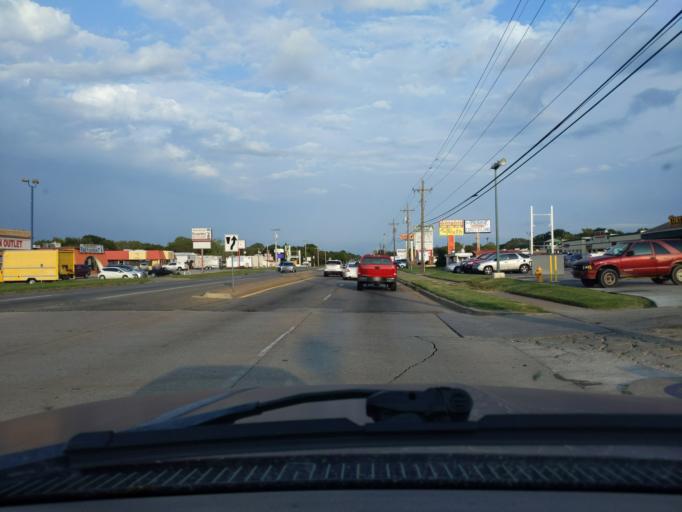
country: US
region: Oklahoma
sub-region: Tulsa County
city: Broken Arrow
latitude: 36.1334
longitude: -95.8496
